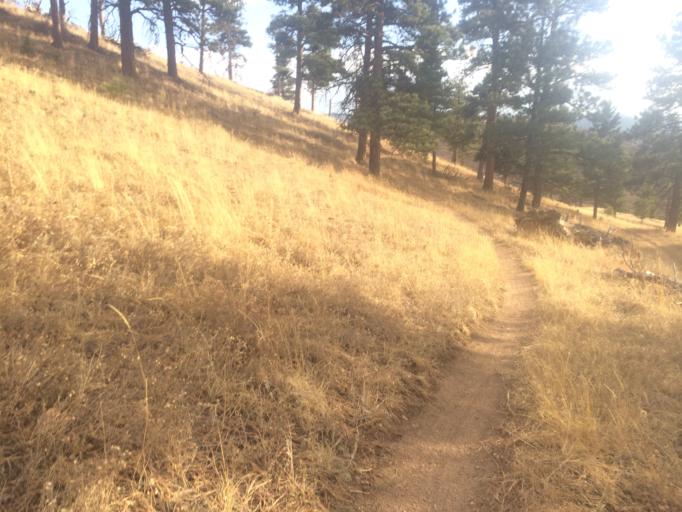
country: US
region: Colorado
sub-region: Boulder County
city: Coal Creek
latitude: 39.9572
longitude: -105.3407
